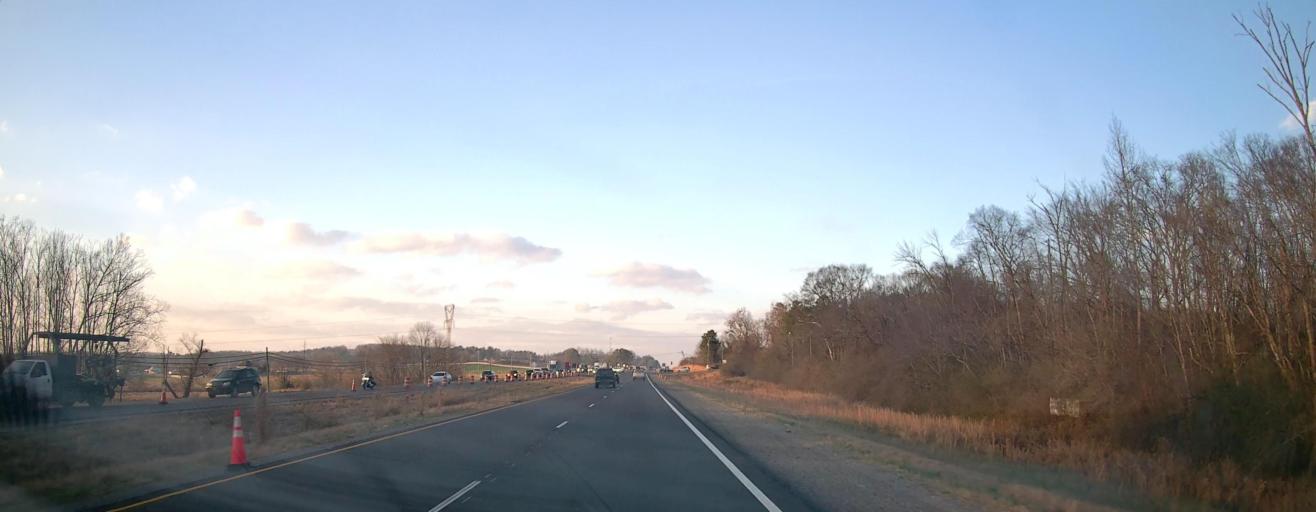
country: US
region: Alabama
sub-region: Calhoun County
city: Alexandria
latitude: 33.7369
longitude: -85.8815
